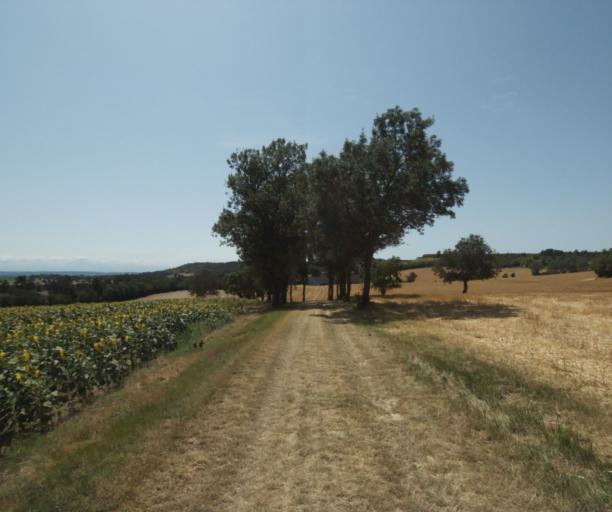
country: FR
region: Midi-Pyrenees
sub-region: Departement de la Haute-Garonne
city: Saint-Felix-Lauragais
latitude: 43.4260
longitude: 1.8839
